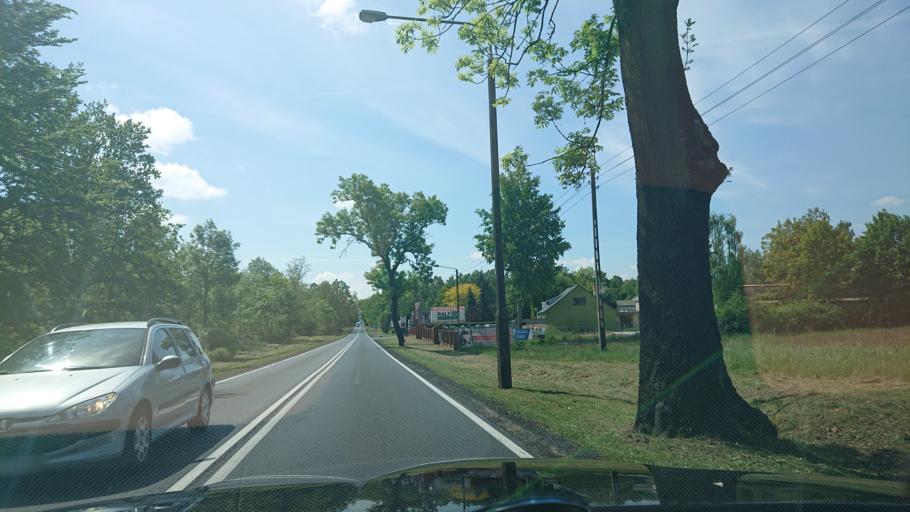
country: PL
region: Greater Poland Voivodeship
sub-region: Powiat gnieznienski
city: Gniezno
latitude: 52.4960
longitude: 17.5942
